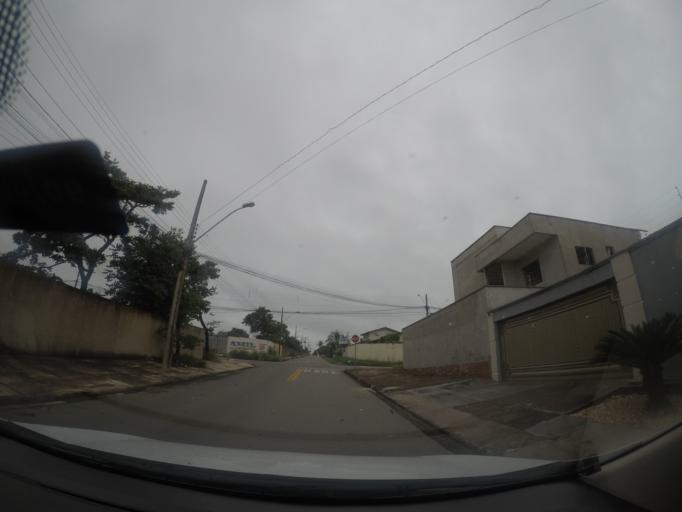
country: BR
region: Goias
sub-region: Goiania
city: Goiania
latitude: -16.7470
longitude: -49.3215
